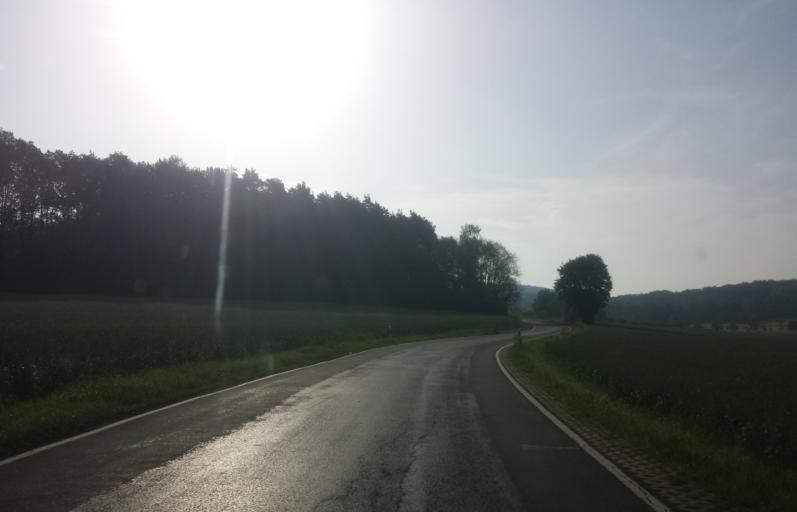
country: DE
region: Bavaria
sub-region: Upper Franconia
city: Ebermannstadt
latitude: 49.7770
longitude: 11.2358
